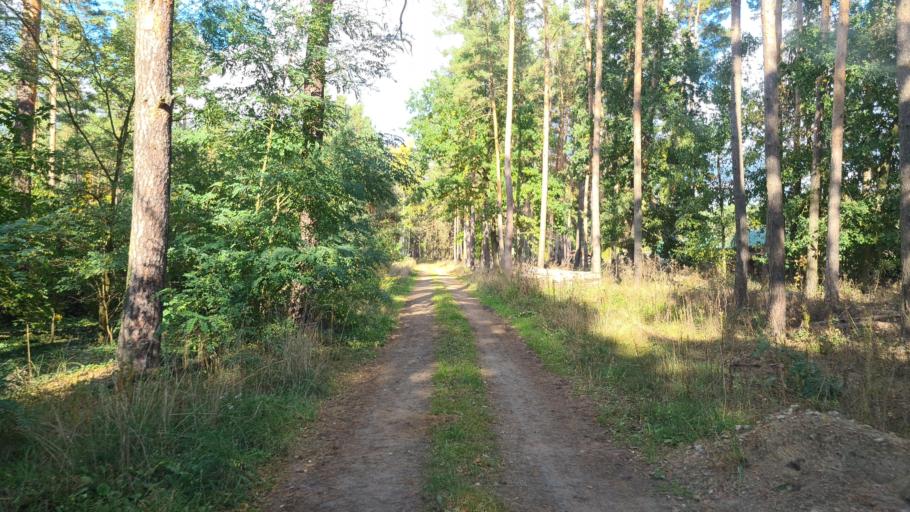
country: DE
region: Brandenburg
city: Vetschau
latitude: 51.7191
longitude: 14.0874
